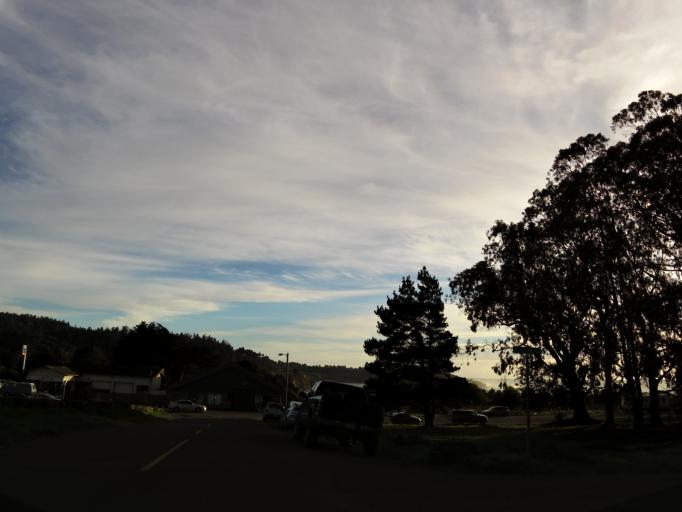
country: US
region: California
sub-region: Mendocino County
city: Fort Bragg
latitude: 39.3059
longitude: -123.7975
